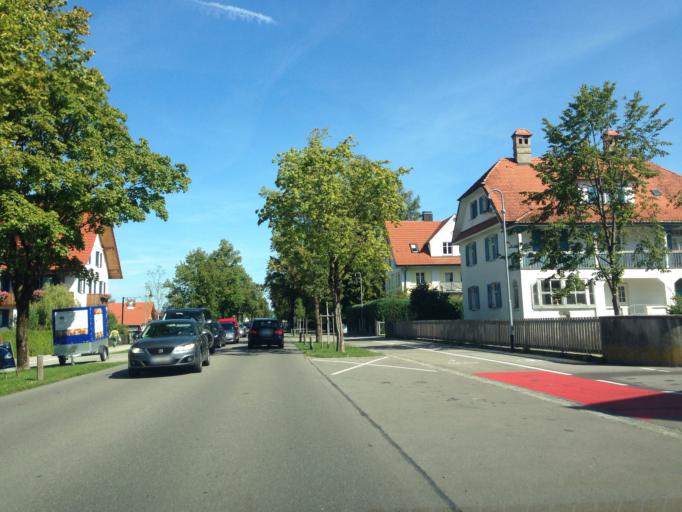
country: DE
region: Bavaria
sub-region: Swabia
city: Fuessen
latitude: 47.5763
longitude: 10.7042
